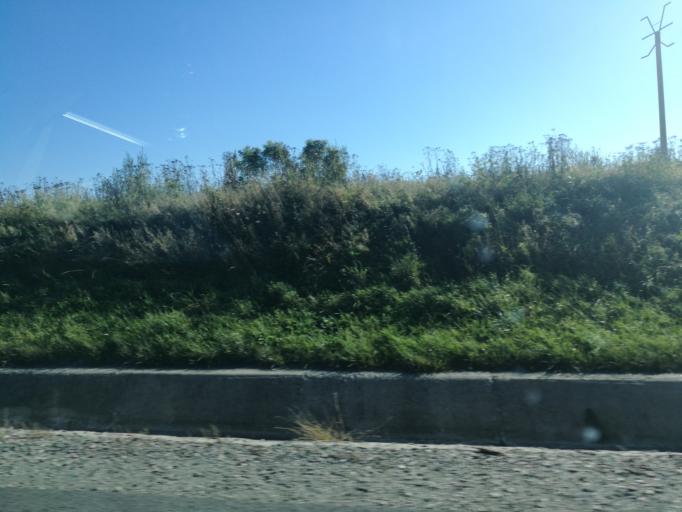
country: RO
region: Brasov
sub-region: Comuna Sercaia
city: Sercaia
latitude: 45.8247
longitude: 25.0978
